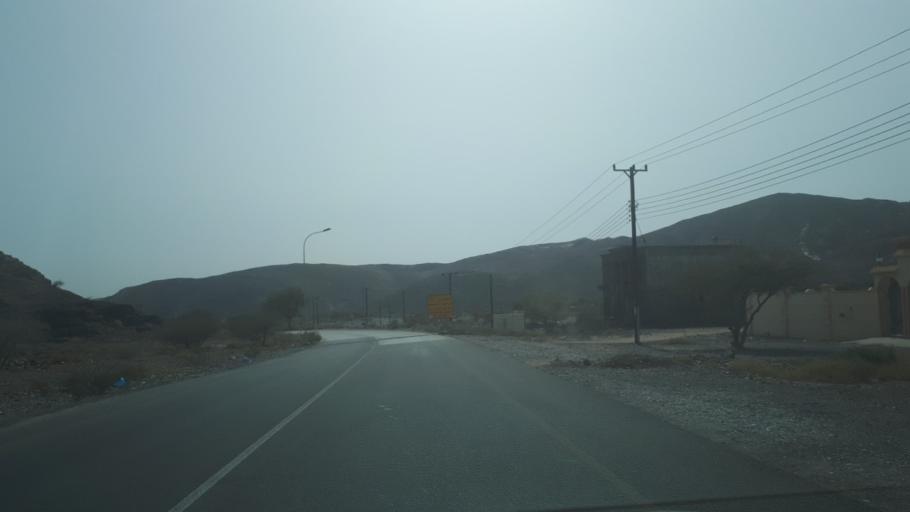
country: OM
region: Muhafazat ad Dakhiliyah
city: Bahla'
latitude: 23.2034
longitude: 56.9475
